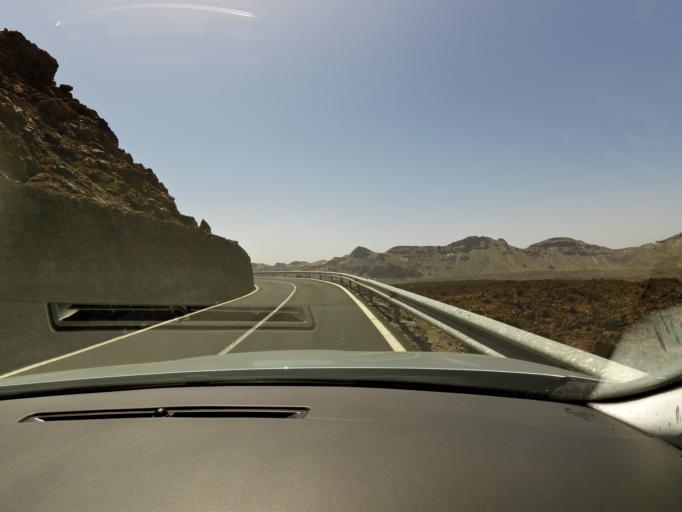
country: ES
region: Canary Islands
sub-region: Provincia de Santa Cruz de Tenerife
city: Vilaflor
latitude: 28.2591
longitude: -16.6057
